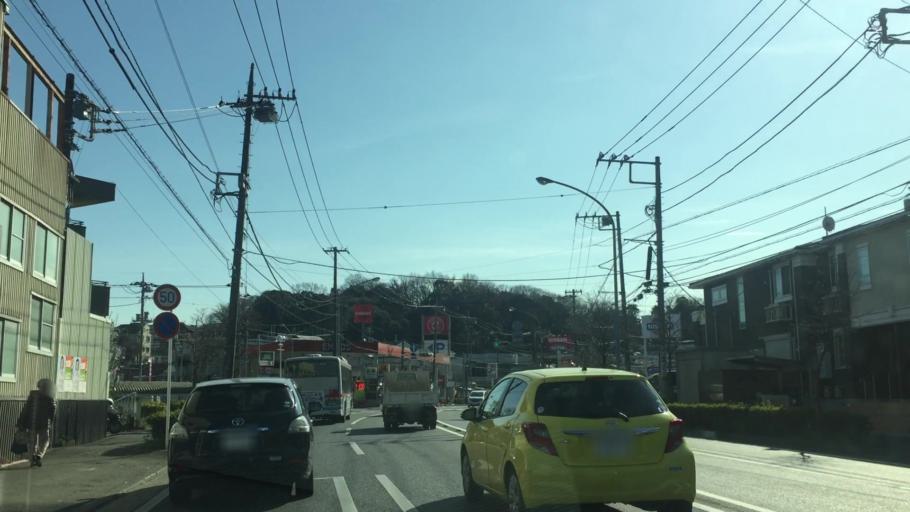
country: JP
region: Kanagawa
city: Yokohama
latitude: 35.3691
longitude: 139.6132
